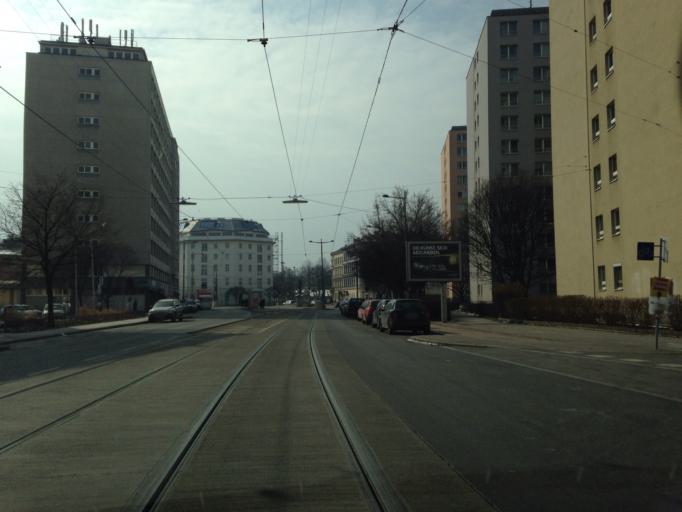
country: AT
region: Vienna
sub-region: Wien Stadt
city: Vienna
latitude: 48.2262
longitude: 16.3852
